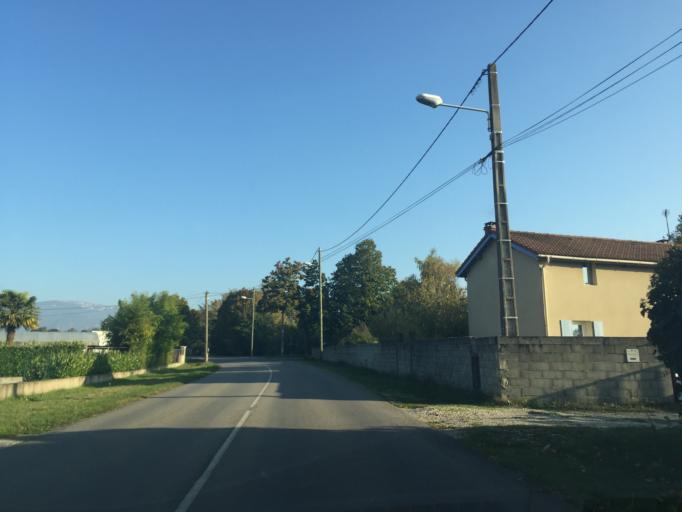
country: FR
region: Rhone-Alpes
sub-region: Departement de la Drome
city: Bourg-de-Peage
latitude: 45.0281
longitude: 5.0697
